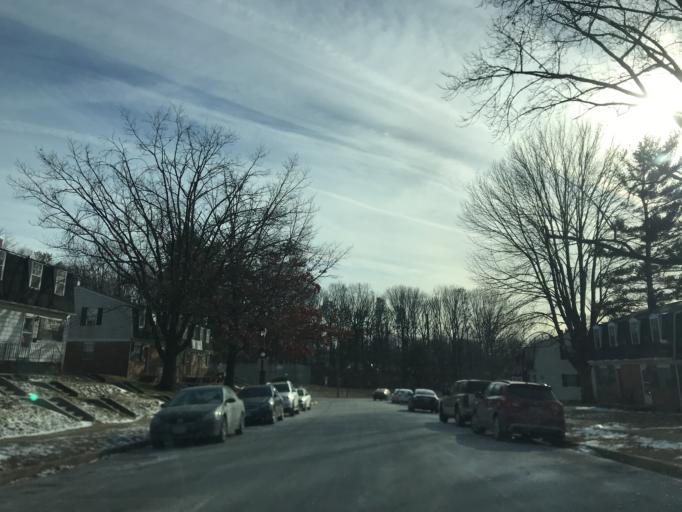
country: US
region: Maryland
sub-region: Baltimore County
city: Rosedale
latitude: 39.3281
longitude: -76.5292
